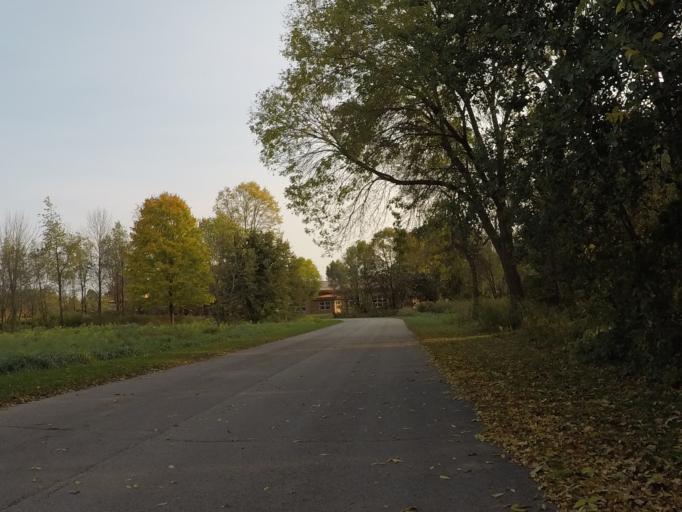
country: US
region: Wisconsin
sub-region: Dane County
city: Verona
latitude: 42.9988
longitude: -89.5284
